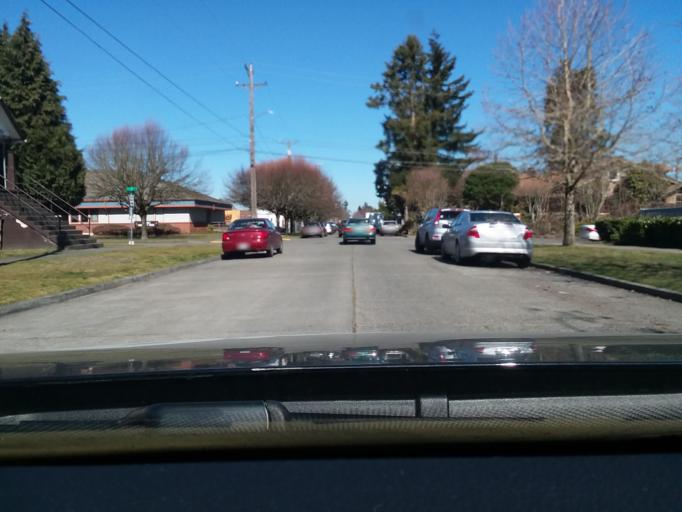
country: US
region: Washington
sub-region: Pierce County
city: Tacoma
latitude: 47.2485
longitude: -122.4524
